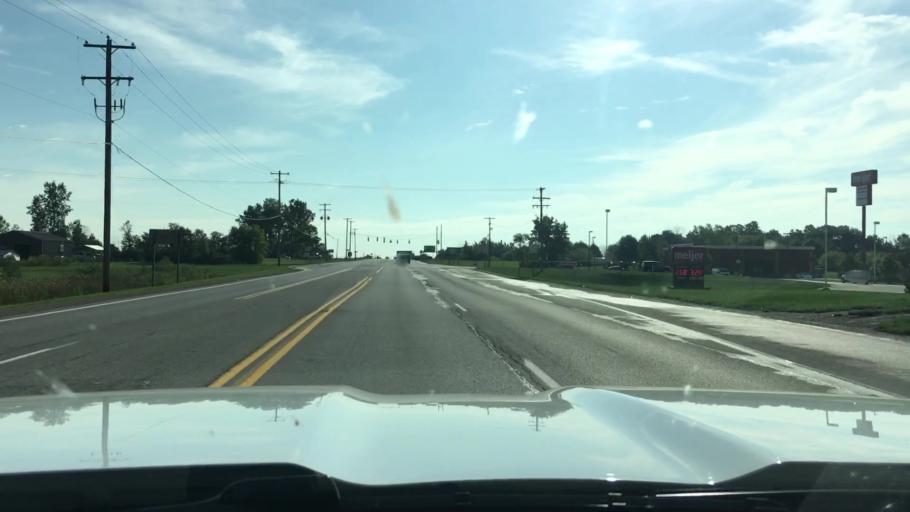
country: US
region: Michigan
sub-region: Kent County
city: Cedar Springs
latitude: 43.2198
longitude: -85.5812
